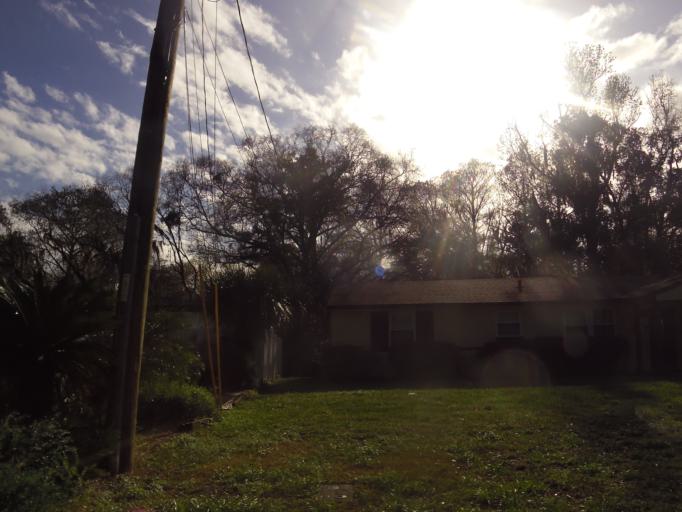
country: US
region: Florida
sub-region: Duval County
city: Jacksonville
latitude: 30.2953
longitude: -81.6179
